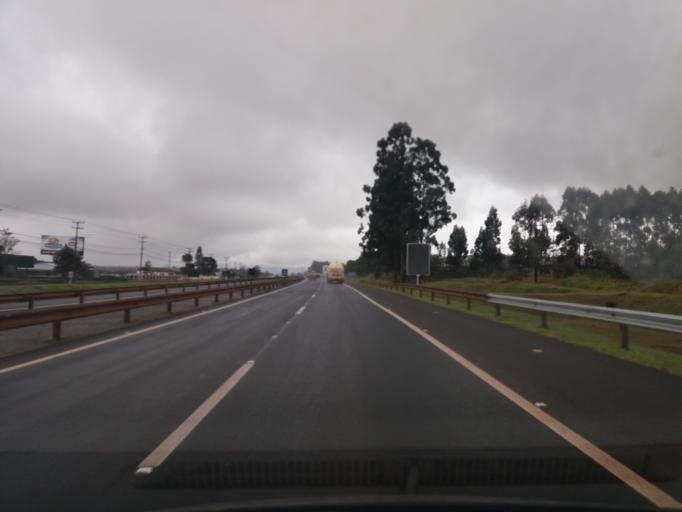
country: BR
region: Parana
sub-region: Cascavel
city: Cascavel
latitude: -24.9957
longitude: -53.5146
